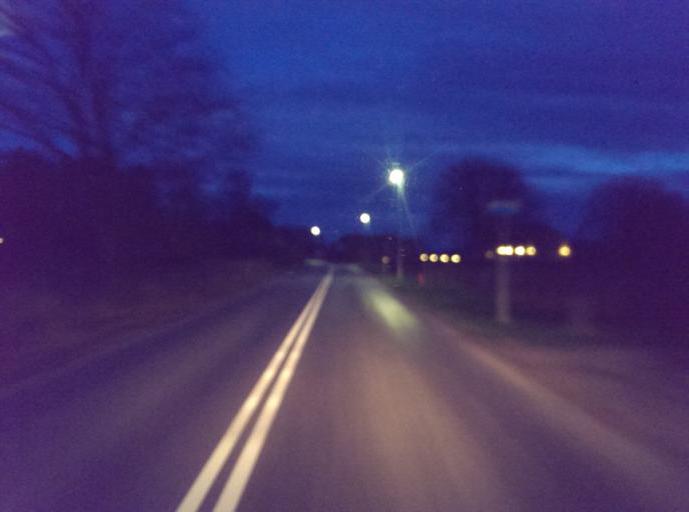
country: DK
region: South Denmark
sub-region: Esbjerg Kommune
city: Tjaereborg
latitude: 55.4765
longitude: 8.5235
